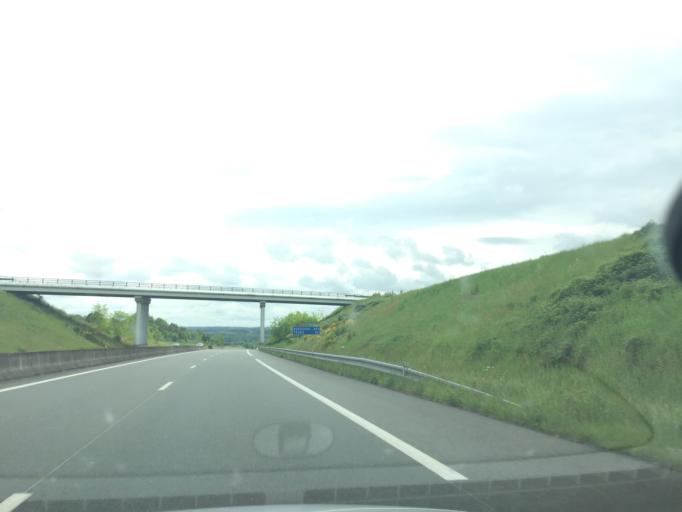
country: FR
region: Pays de la Loire
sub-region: Departement de la Sarthe
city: Luceau
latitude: 47.6823
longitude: 0.3690
